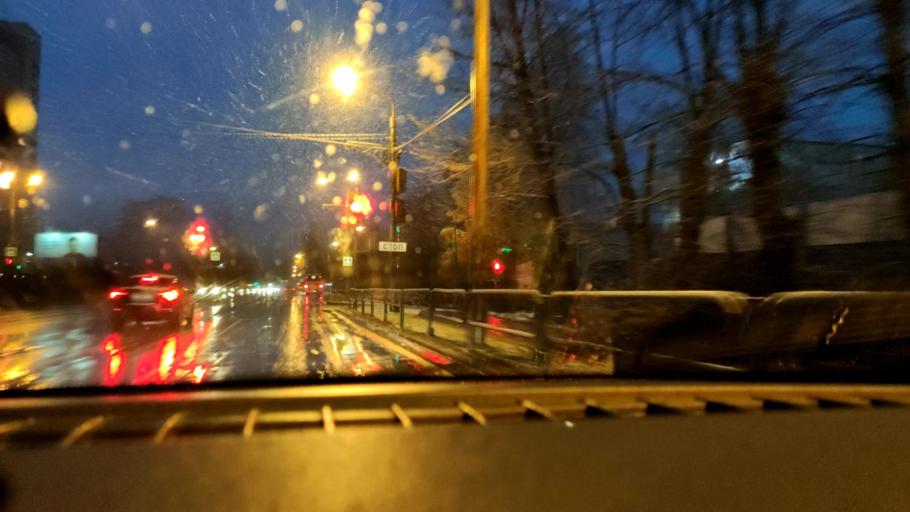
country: RU
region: Perm
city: Kondratovo
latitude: 58.0392
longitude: 56.0321
